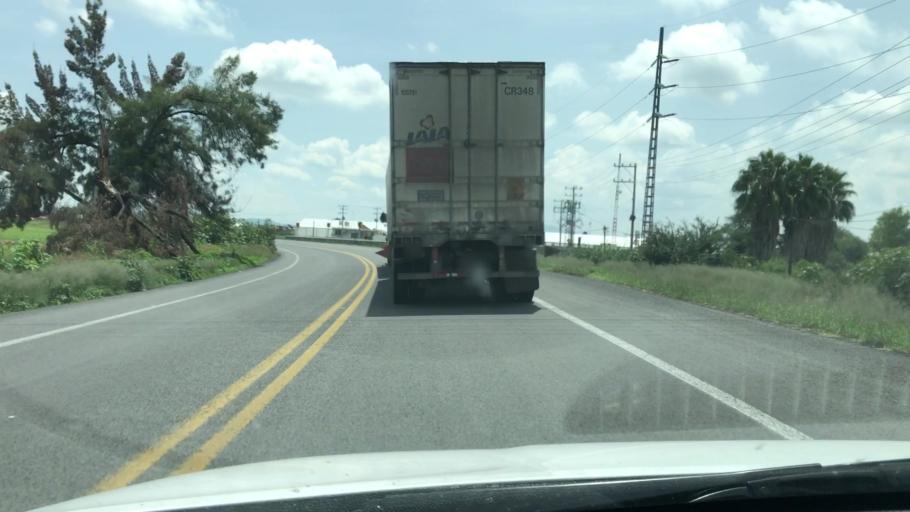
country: MX
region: Michoacan
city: Tanhuato de Guerrero
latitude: 20.2825
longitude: -102.3446
